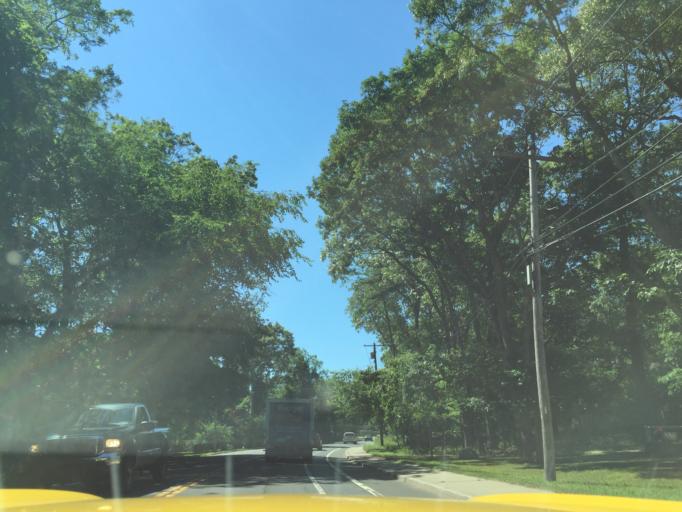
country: US
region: New York
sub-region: Suffolk County
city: Sag Harbor
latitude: 40.9934
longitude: -72.2742
